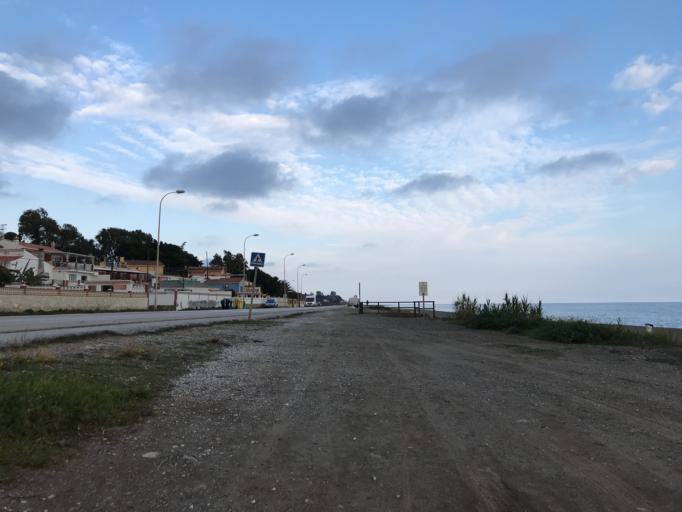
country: ES
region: Andalusia
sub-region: Provincia de Malaga
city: Valdes
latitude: 36.7150
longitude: -4.2035
